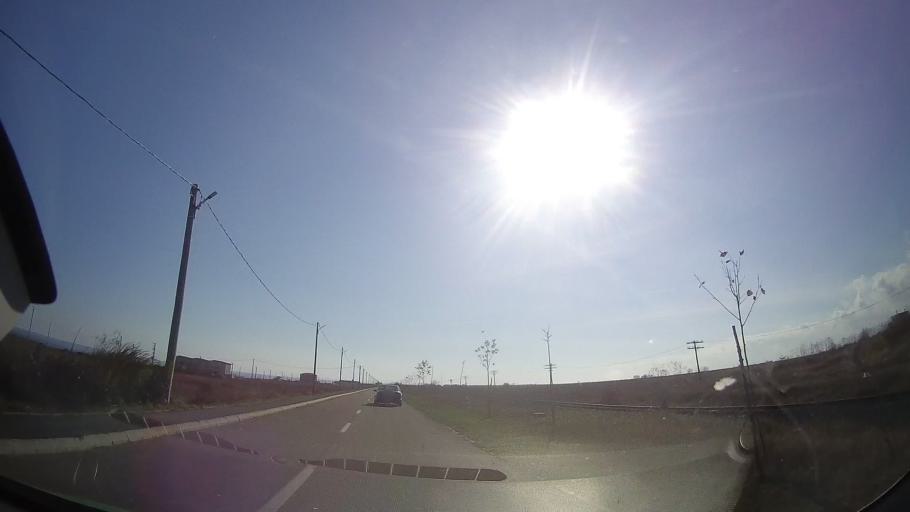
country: RO
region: Constanta
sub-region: Comuna Costinesti
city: Schitu
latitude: 43.9335
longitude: 28.6309
